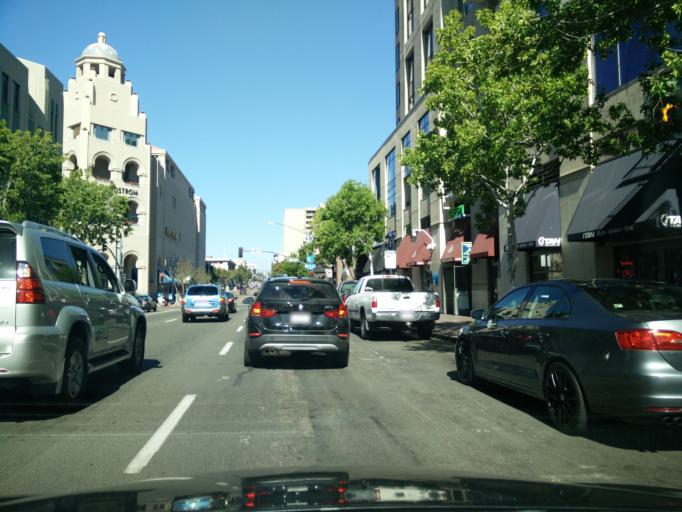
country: US
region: California
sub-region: San Diego County
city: San Diego
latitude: 32.7125
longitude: -117.1645
